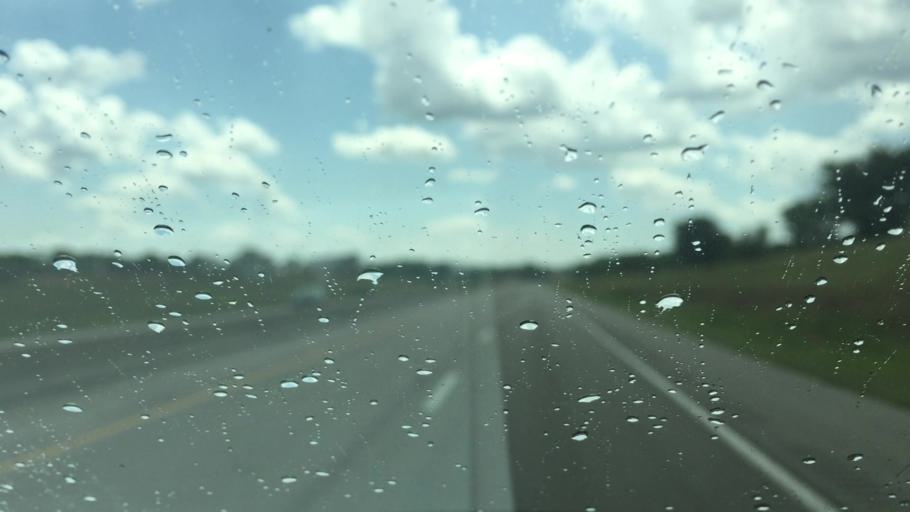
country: US
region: Kansas
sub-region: Shawnee County
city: Topeka
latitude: 38.9748
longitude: -95.7107
